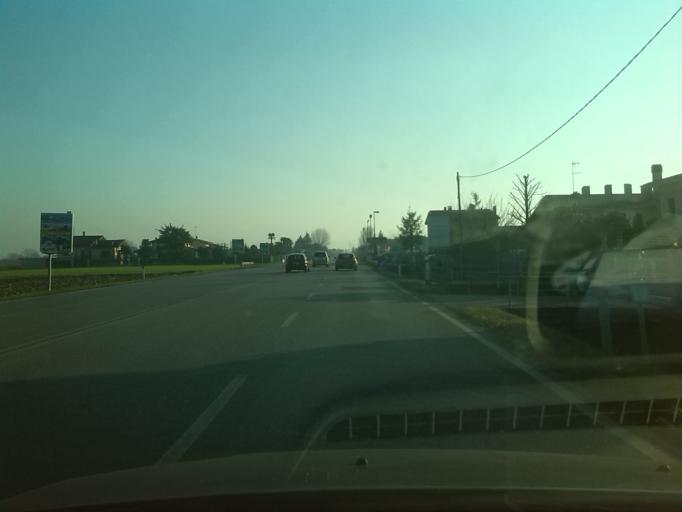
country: IT
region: Friuli Venezia Giulia
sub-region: Provincia di Udine
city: Pertegada
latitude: 45.7271
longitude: 13.0457
